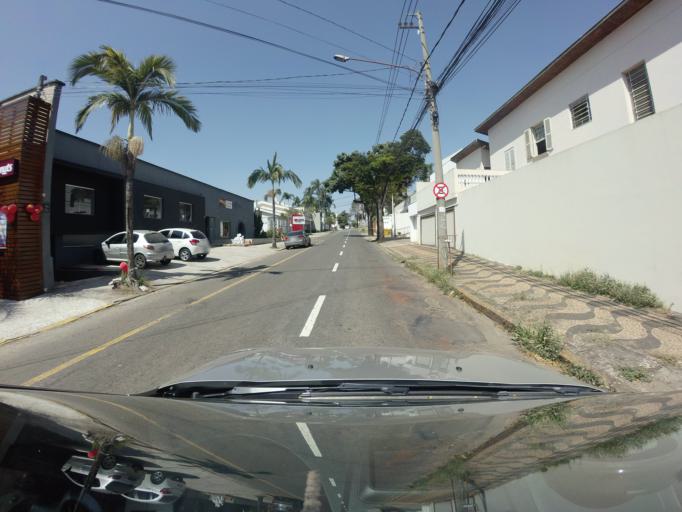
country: BR
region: Sao Paulo
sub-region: Piracicaba
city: Piracicaba
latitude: -22.7191
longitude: -47.6438
